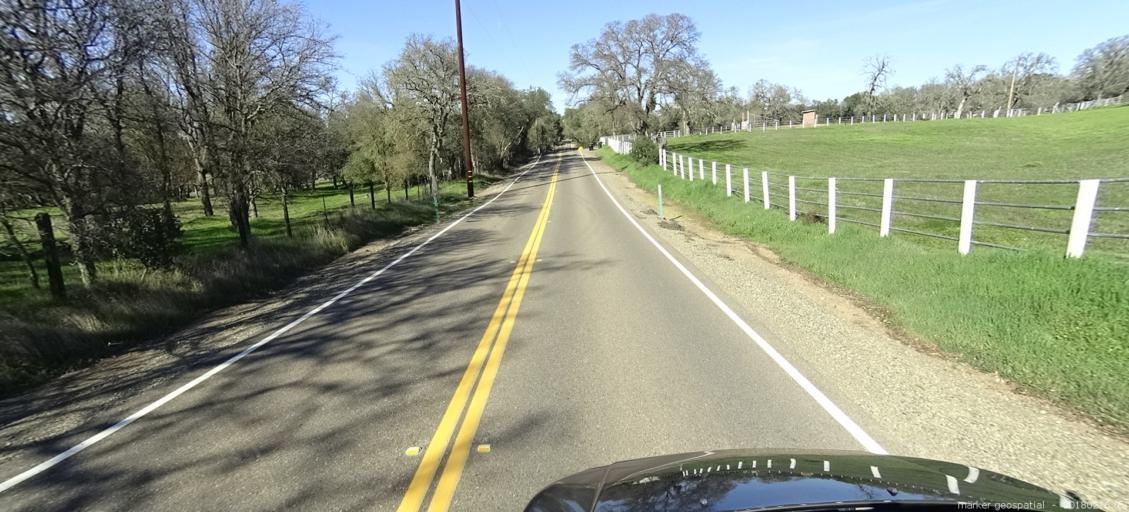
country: US
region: California
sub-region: Sacramento County
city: Rancho Murieta
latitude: 38.5264
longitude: -121.1041
